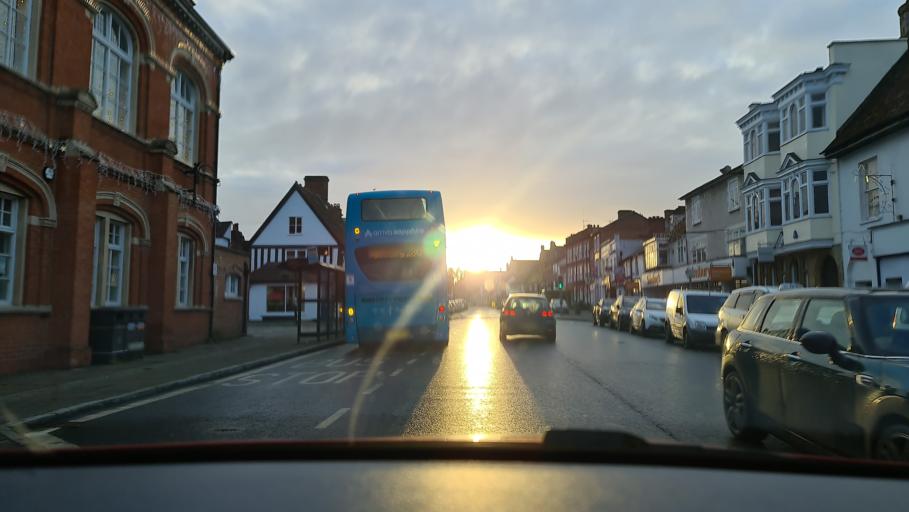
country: GB
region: England
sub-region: Oxfordshire
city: Thame
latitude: 51.7477
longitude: -0.9787
